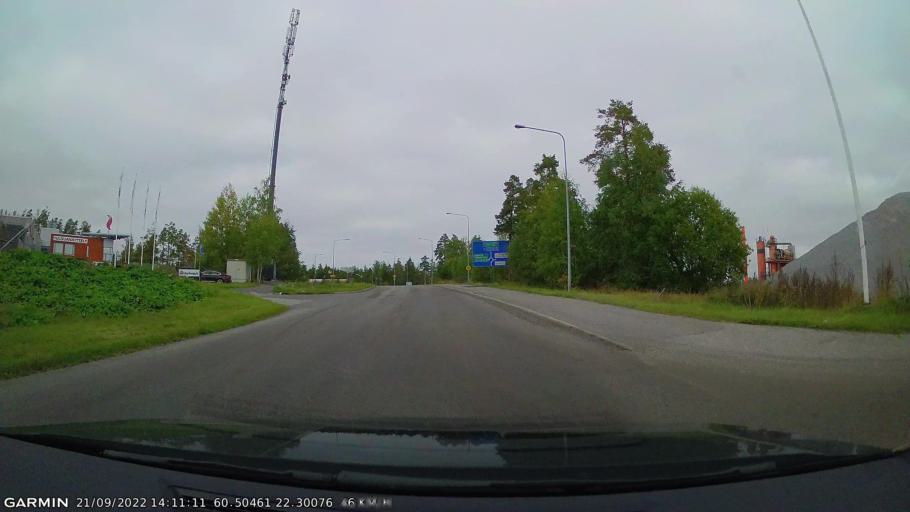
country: FI
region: Varsinais-Suomi
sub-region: Turku
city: Turku
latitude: 60.5044
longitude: 22.3013
